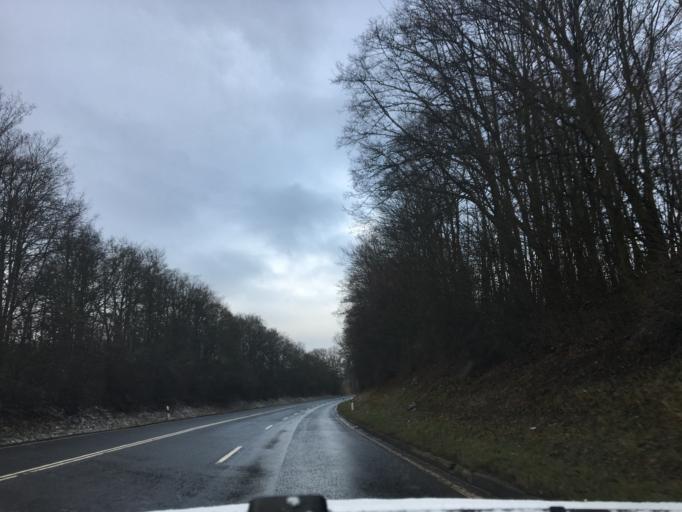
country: DE
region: Rheinland-Pfalz
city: Kirchheimbolanden
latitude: 49.6787
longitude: 8.0110
